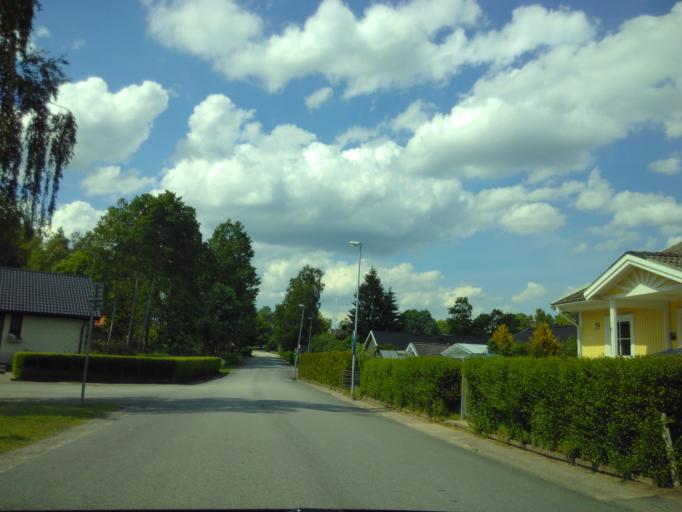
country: SE
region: Vaestra Goetaland
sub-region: Herrljunga Kommun
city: Herrljunga
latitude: 58.0757
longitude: 13.0423
